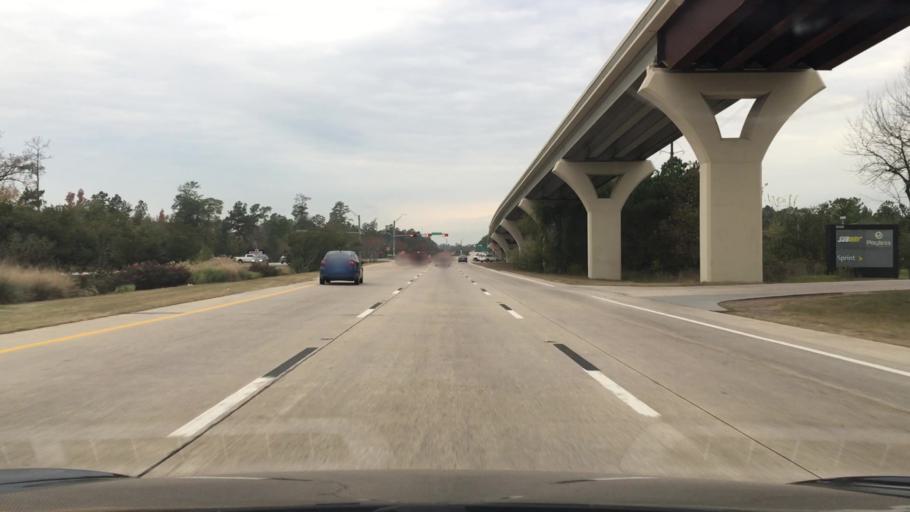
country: US
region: Texas
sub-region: Montgomery County
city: Shenandoah
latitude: 30.2074
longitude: -95.4588
